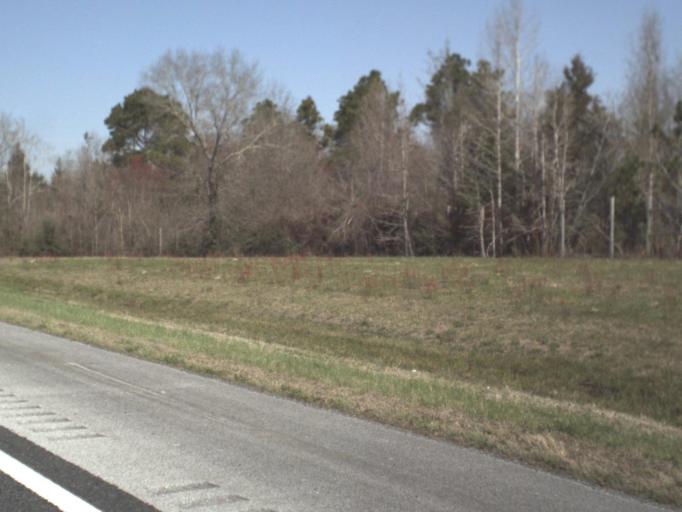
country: US
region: Florida
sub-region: Jackson County
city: Marianna
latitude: 30.6867
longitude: -85.1107
